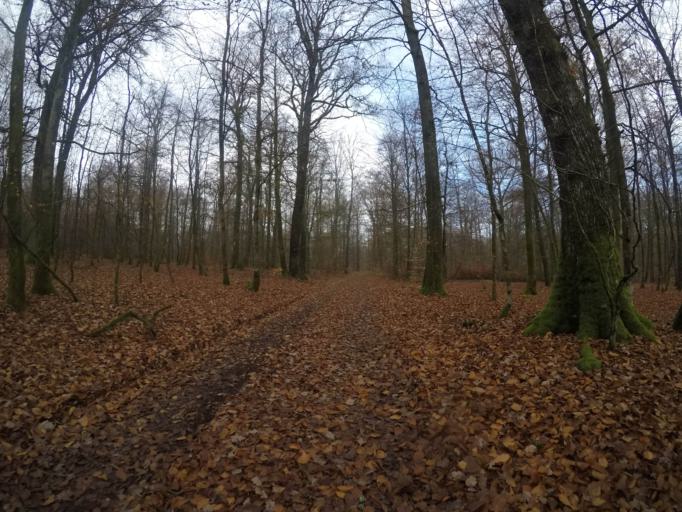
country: BE
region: Wallonia
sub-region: Province du Luxembourg
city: Habay-la-Vieille
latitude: 49.7451
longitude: 5.5932
